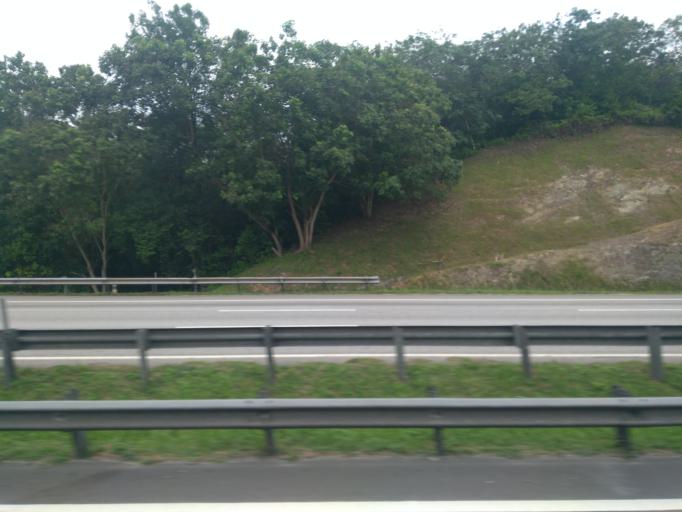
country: MY
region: Negeri Sembilan
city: Tampin
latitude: 2.4668
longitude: 102.1487
